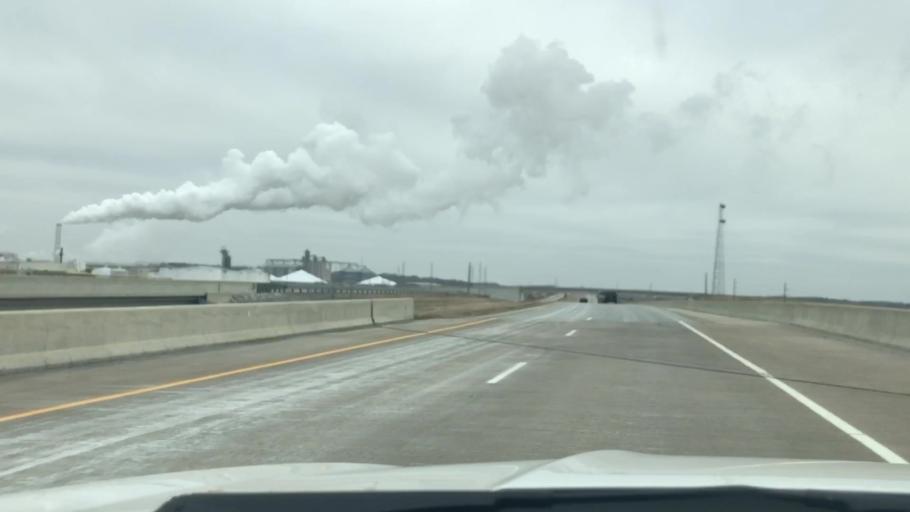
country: US
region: Indiana
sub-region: Cass County
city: Dunkirk
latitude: 40.7123
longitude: -86.4396
